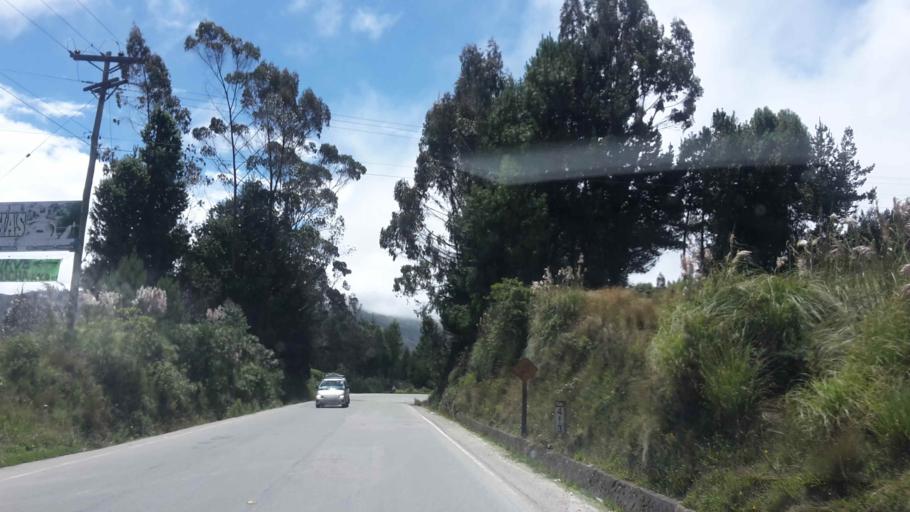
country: BO
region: Cochabamba
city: Colomi
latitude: -17.2660
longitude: -65.8837
